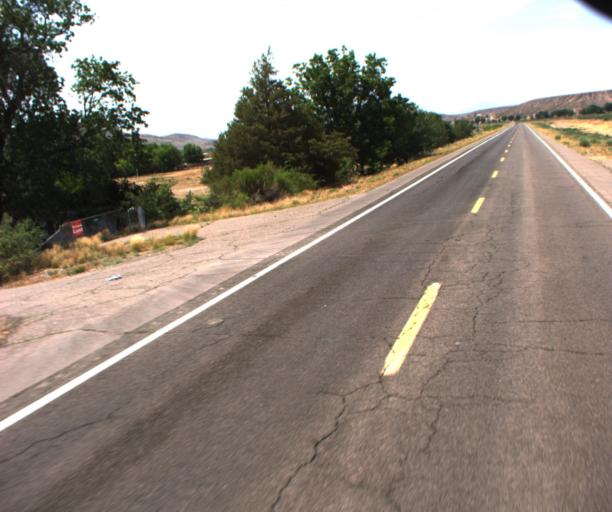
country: US
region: Arizona
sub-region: Greenlee County
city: Clifton
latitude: 32.8497
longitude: -109.1817
